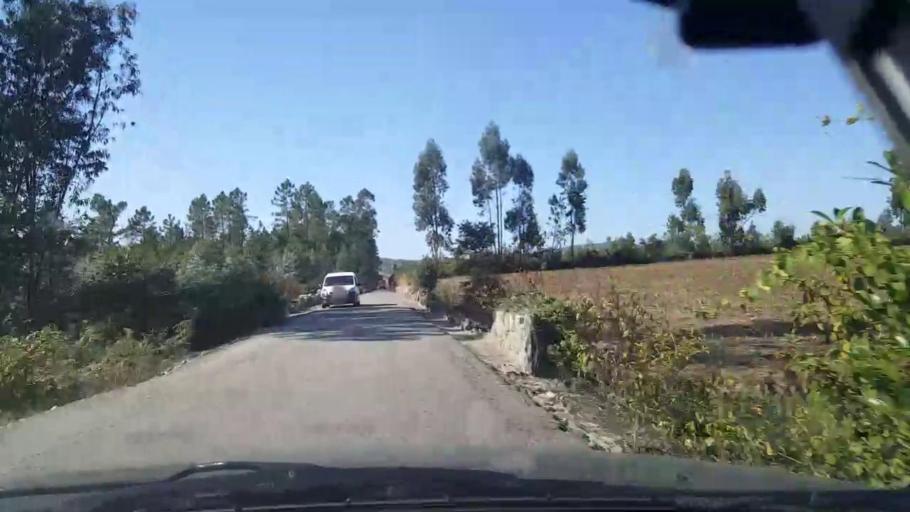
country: PT
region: Braga
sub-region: Vila Nova de Famalicao
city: Ribeirao
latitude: 41.3562
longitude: -8.6394
